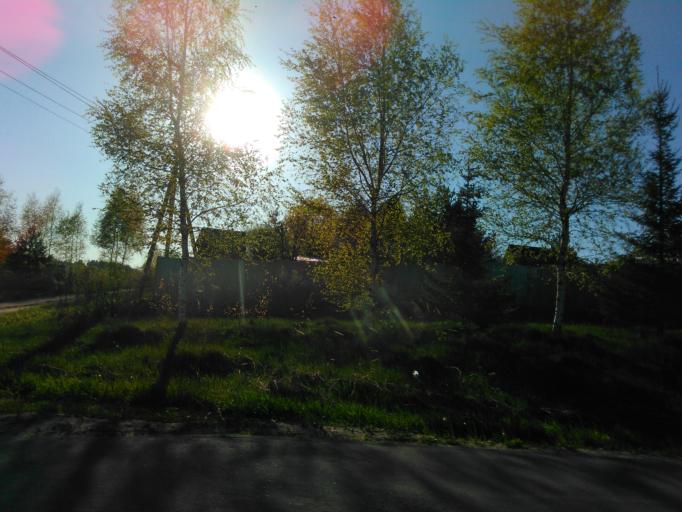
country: RU
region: Moskovskaya
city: Solnechnogorsk
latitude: 56.1212
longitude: 36.9298
